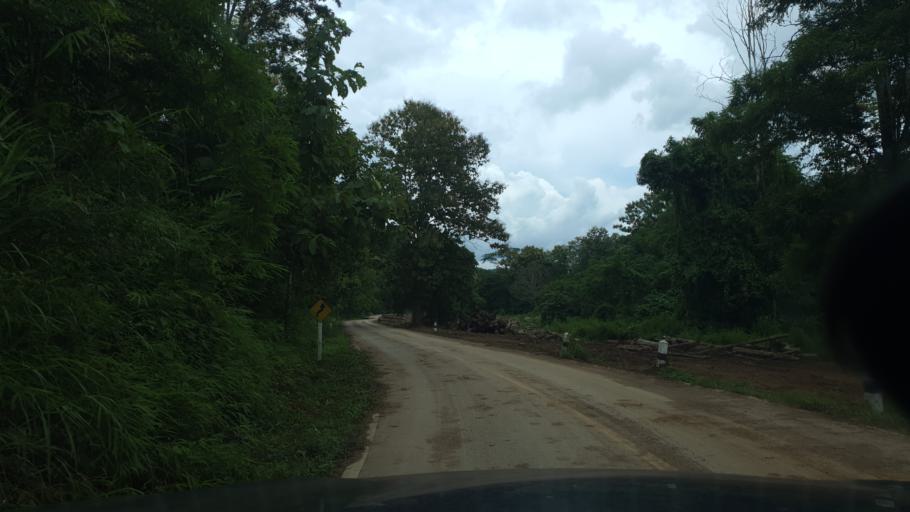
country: TH
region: Lampang
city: Hang Chat
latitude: 18.3719
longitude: 99.2605
